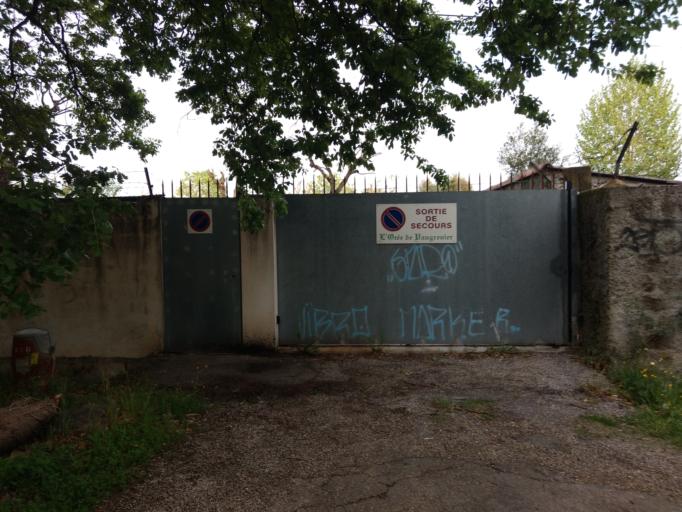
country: FR
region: Provence-Alpes-Cote d'Azur
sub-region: Departement des Alpes-Maritimes
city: Biot
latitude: 43.6207
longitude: 7.1244
